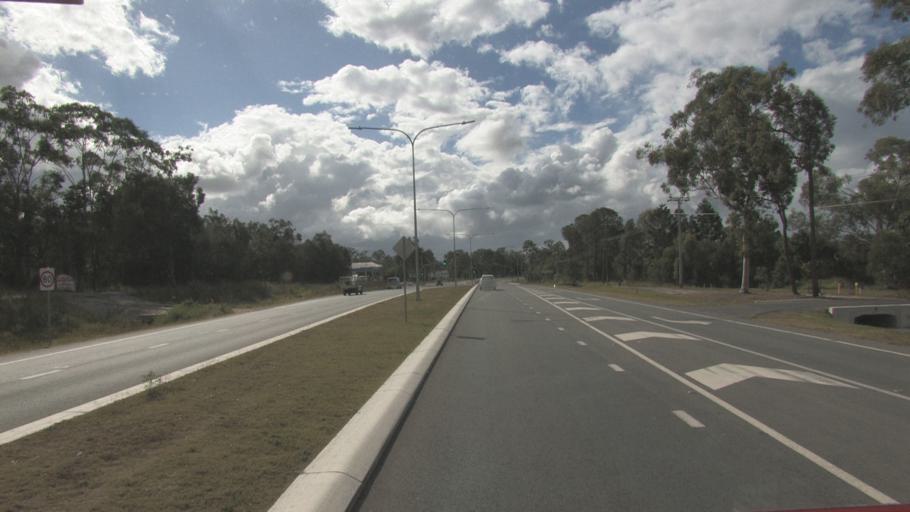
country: AU
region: Queensland
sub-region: Logan
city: Logan Reserve
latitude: -27.7106
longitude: 153.0935
